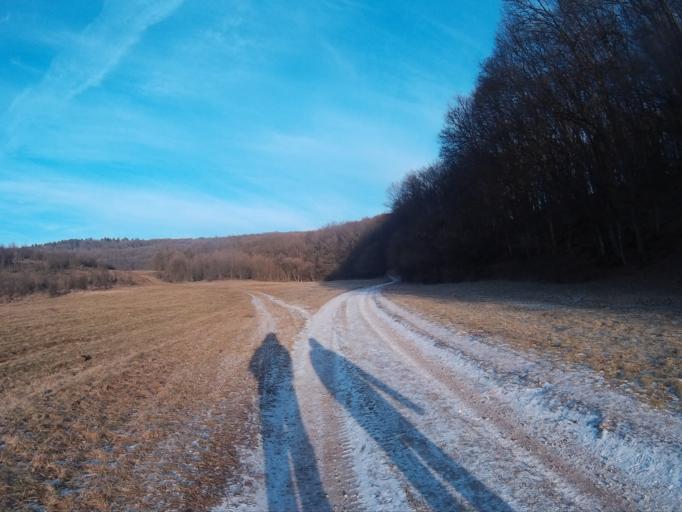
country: SK
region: Kosicky
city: Roznava
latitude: 48.5458
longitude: 20.6480
